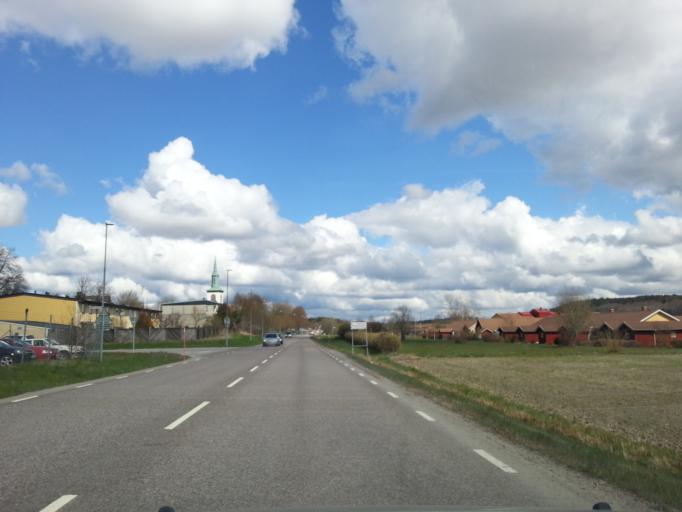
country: SE
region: Vaestra Goetaland
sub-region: Kungalvs Kommun
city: Kungalv
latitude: 57.8587
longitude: 11.9188
